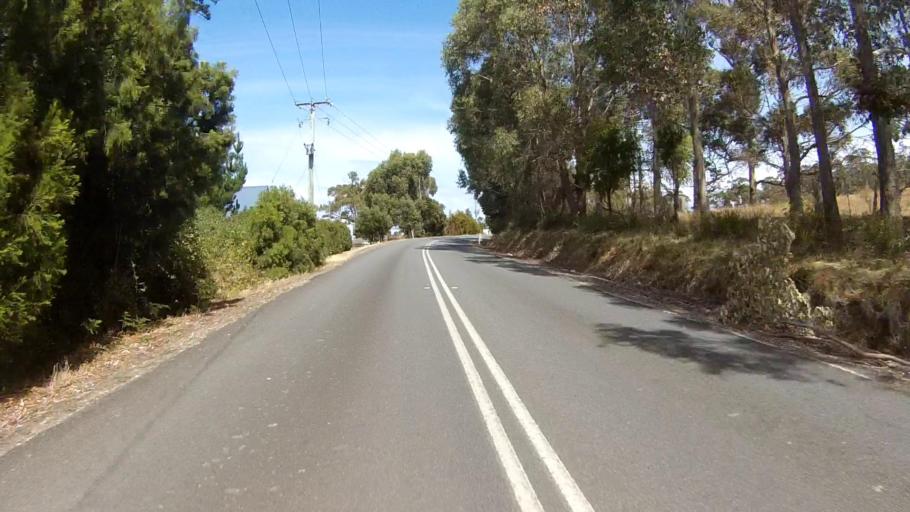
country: AU
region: Tasmania
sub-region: Huon Valley
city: Cygnet
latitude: -43.2740
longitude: 147.1540
